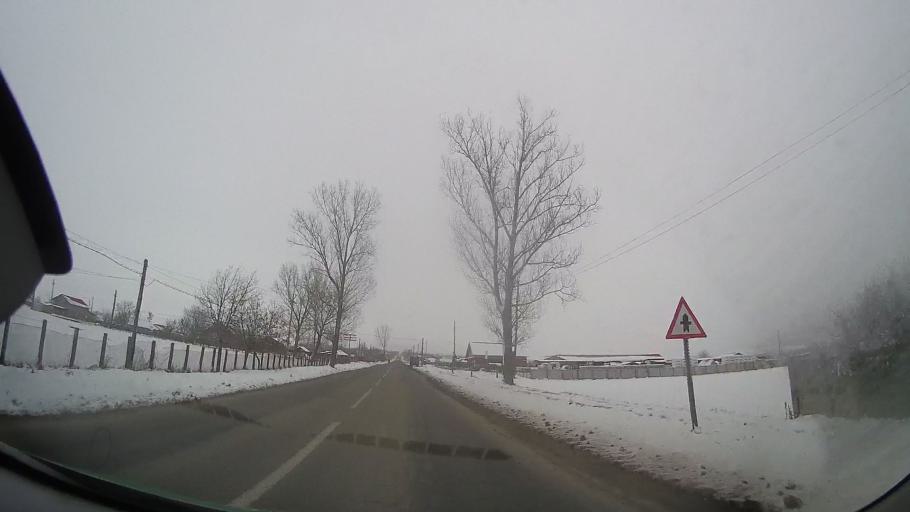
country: RO
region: Vaslui
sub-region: Comuna Todiresti
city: Todiresti
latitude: 46.8387
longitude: 27.3966
